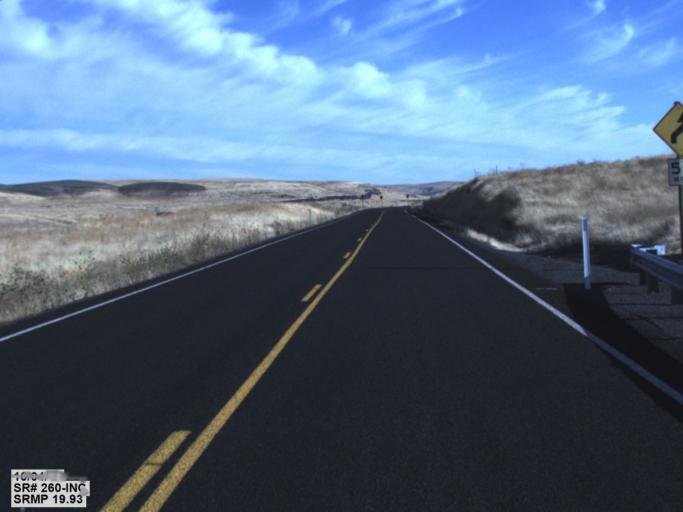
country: US
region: Washington
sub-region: Franklin County
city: Connell
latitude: 46.6295
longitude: -118.6437
